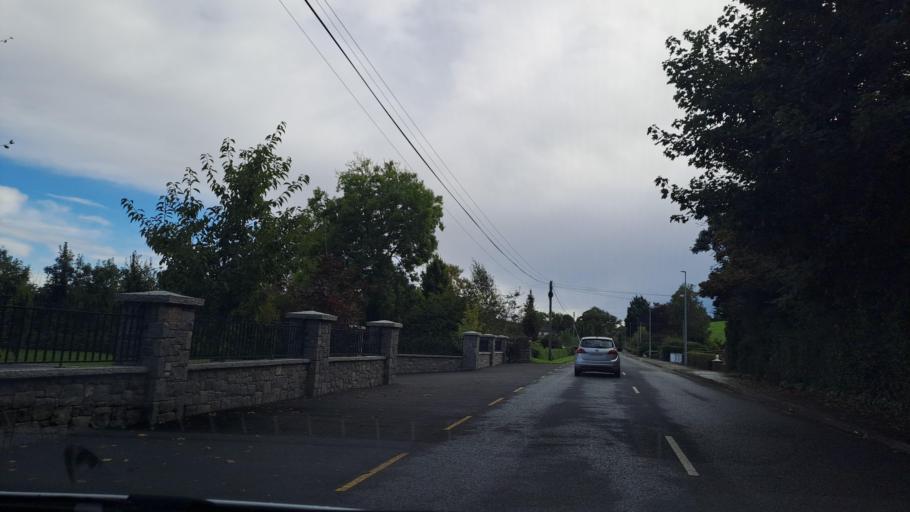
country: IE
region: Ulster
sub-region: County Monaghan
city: Carrickmacross
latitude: 53.9635
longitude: -6.7089
